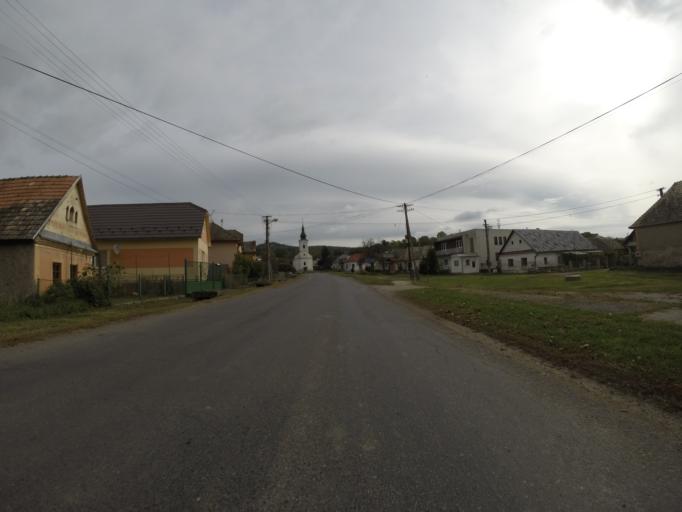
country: SK
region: Banskobystricky
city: Rimavska Sobota
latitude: 48.4701
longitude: 20.0997
